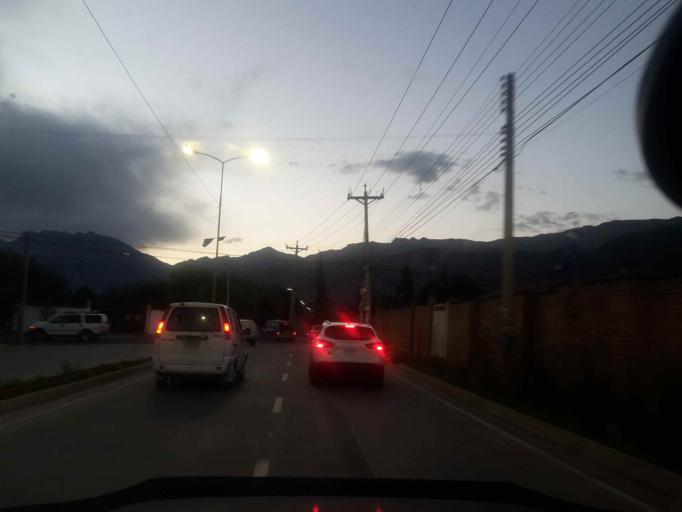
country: BO
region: Cochabamba
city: Cochabamba
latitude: -17.3423
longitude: -66.2034
